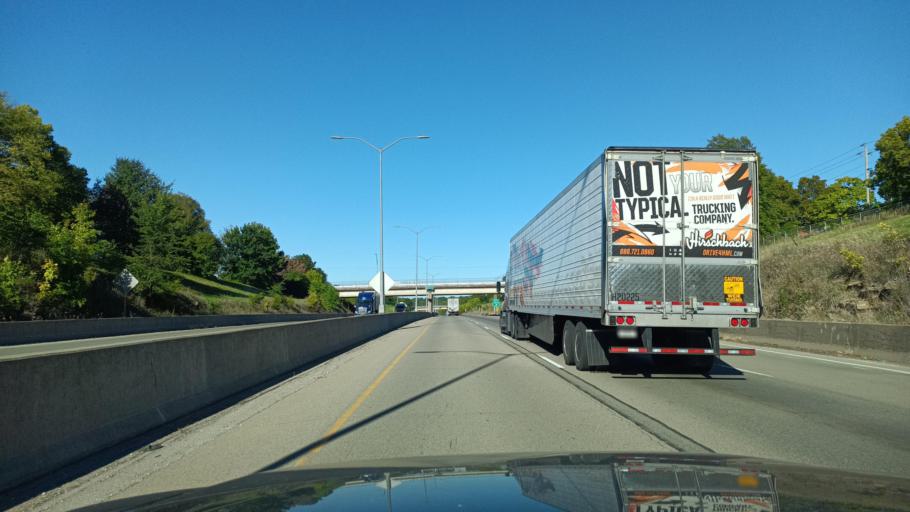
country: US
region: Iowa
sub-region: Des Moines County
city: Burlington
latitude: 40.8148
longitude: -91.1050
